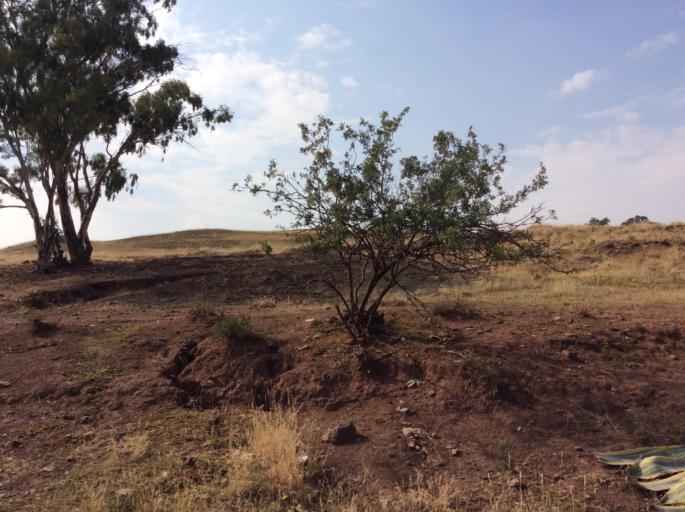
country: LS
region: Mafeteng
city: Mafeteng
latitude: -29.9875
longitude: 27.0030
